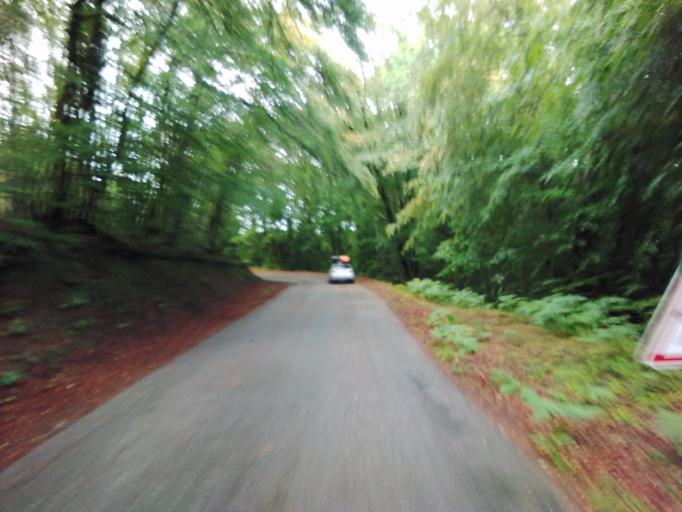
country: FR
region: Bourgogne
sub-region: Departement de la Nievre
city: Lormes
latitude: 47.2984
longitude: 3.8879
